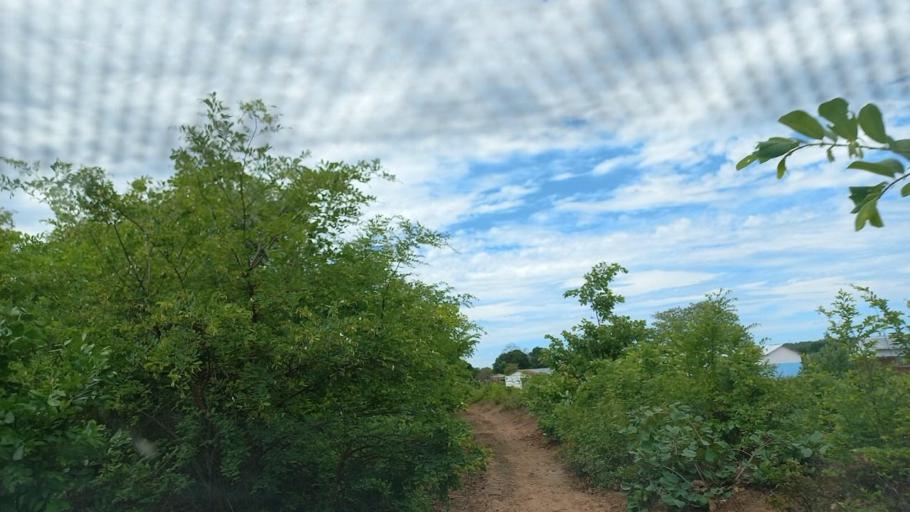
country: ZM
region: North-Western
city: Kabompo
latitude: -13.5522
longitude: 24.2713
